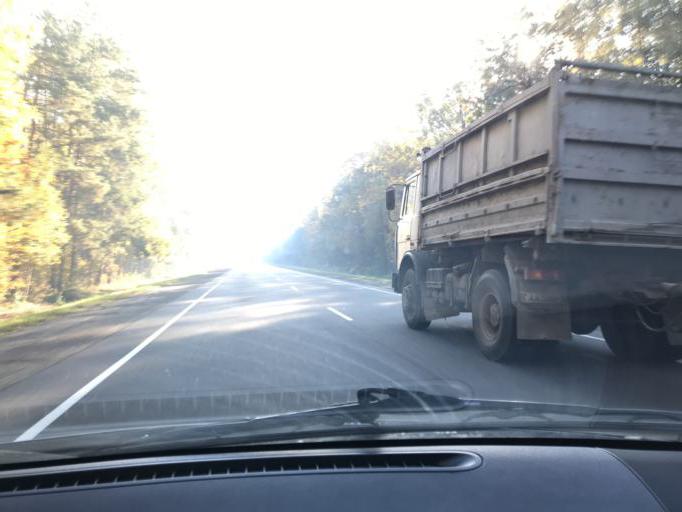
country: BY
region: Brest
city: Horad Luninyets
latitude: 52.2844
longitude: 26.8068
